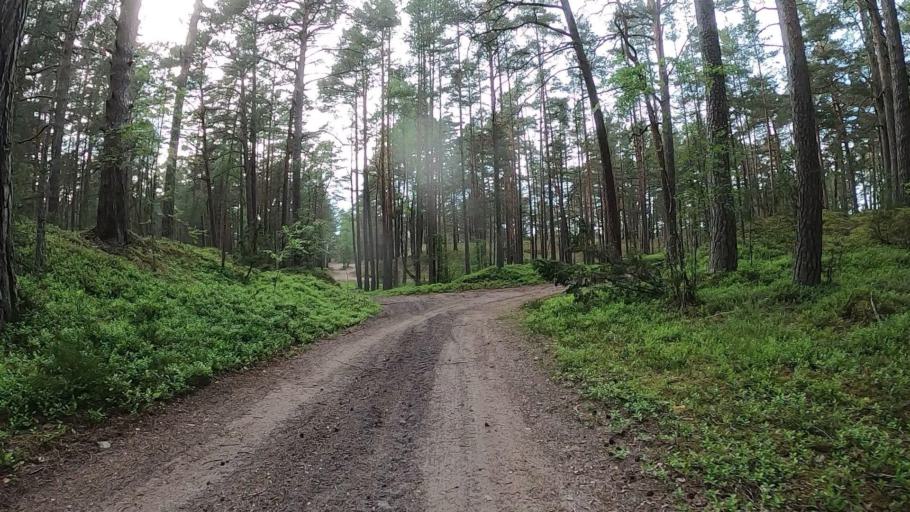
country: LV
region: Riga
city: Jaunciems
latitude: 57.0771
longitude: 24.1291
